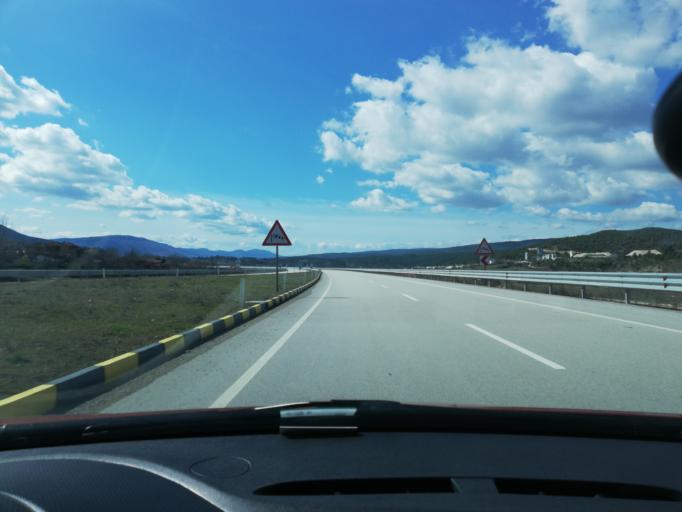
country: TR
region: Kastamonu
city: Igdir
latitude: 41.2299
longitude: 33.0153
